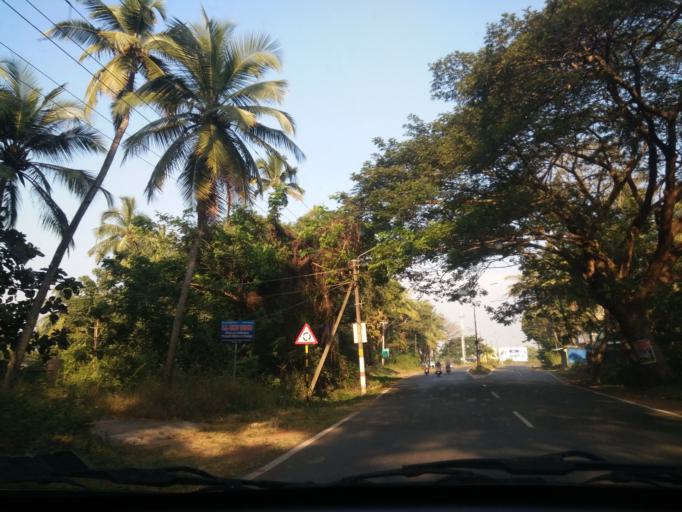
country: IN
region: Goa
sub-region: South Goa
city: Chinchinim
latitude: 15.2178
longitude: 73.9799
